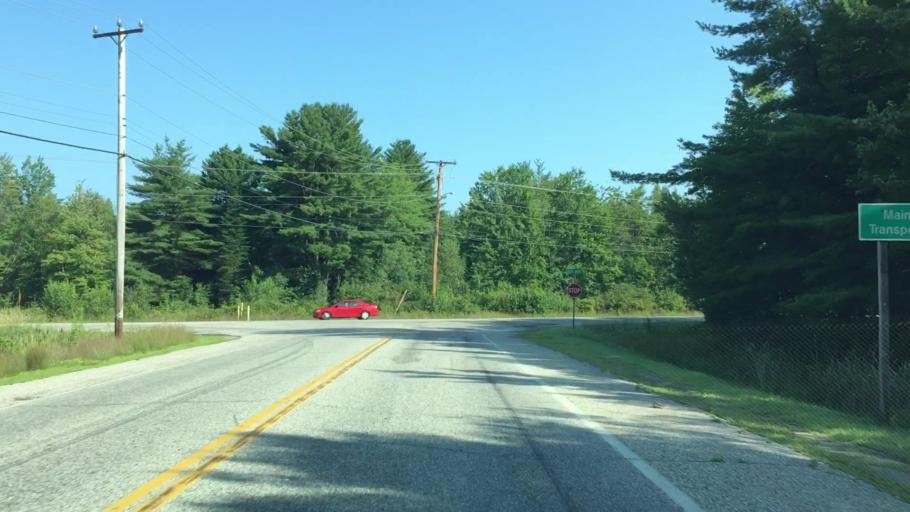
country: US
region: Maine
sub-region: Androscoggin County
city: Minot
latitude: 44.0471
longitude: -70.2958
